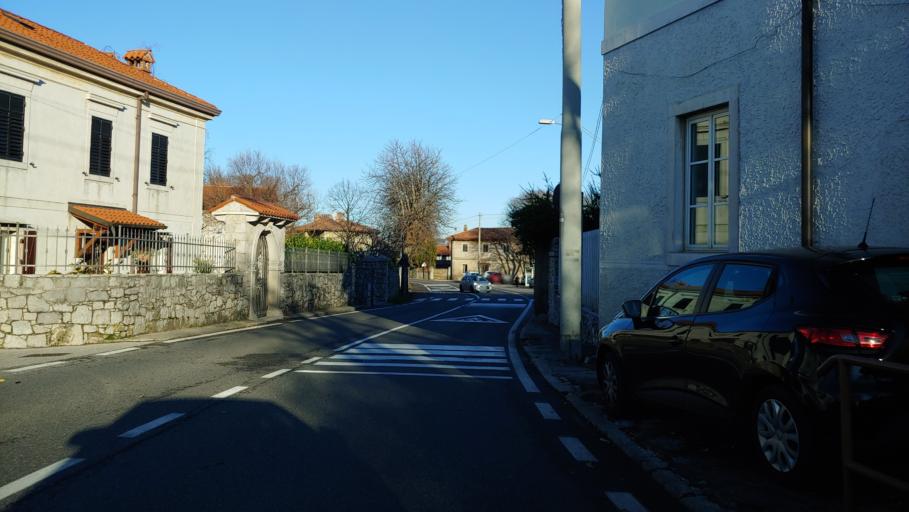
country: IT
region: Friuli Venezia Giulia
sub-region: Provincia di Trieste
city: Villa Opicina
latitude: 45.6718
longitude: 13.8254
